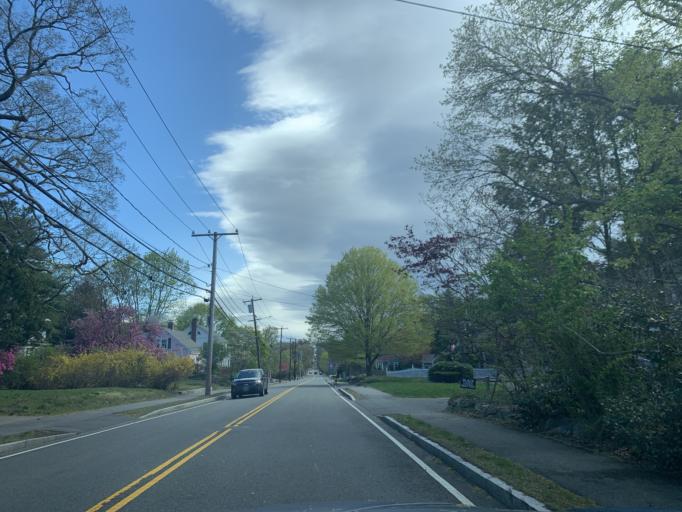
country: US
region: Massachusetts
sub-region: Norfolk County
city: Milton
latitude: 42.2432
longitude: -71.0972
